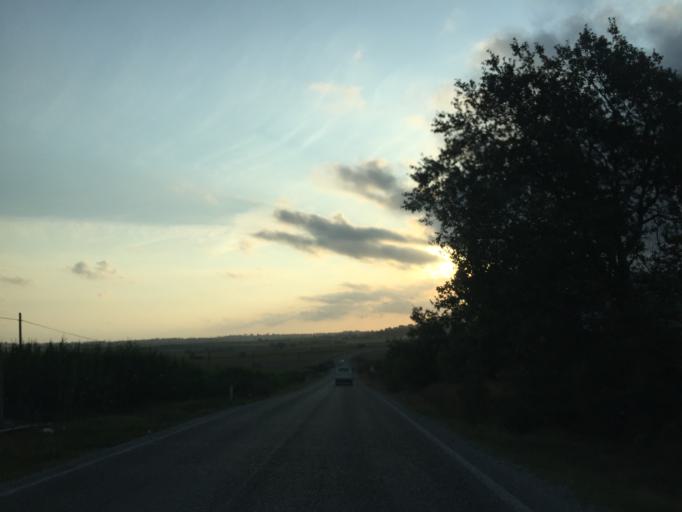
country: TR
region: Balikesir
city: Tutuncu
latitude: 40.1089
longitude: 27.7120
